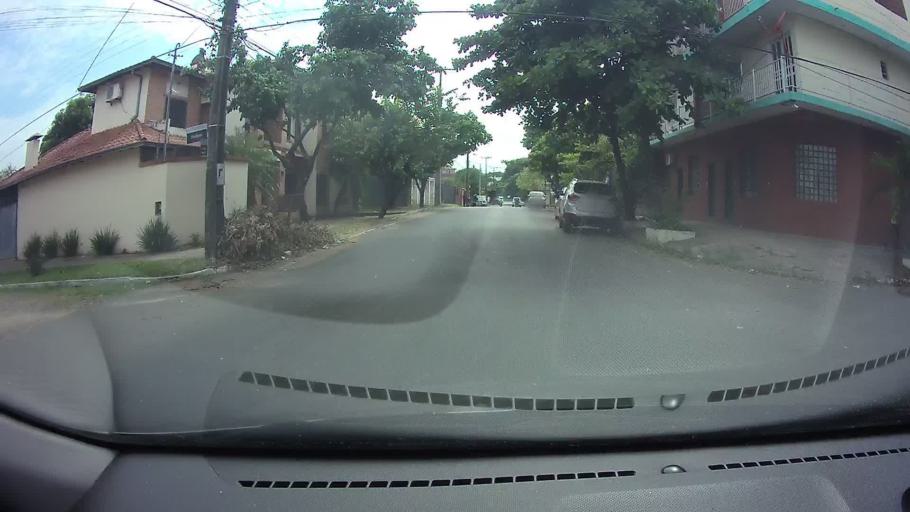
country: PY
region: Central
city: Fernando de la Mora
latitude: -25.3029
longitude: -57.5420
